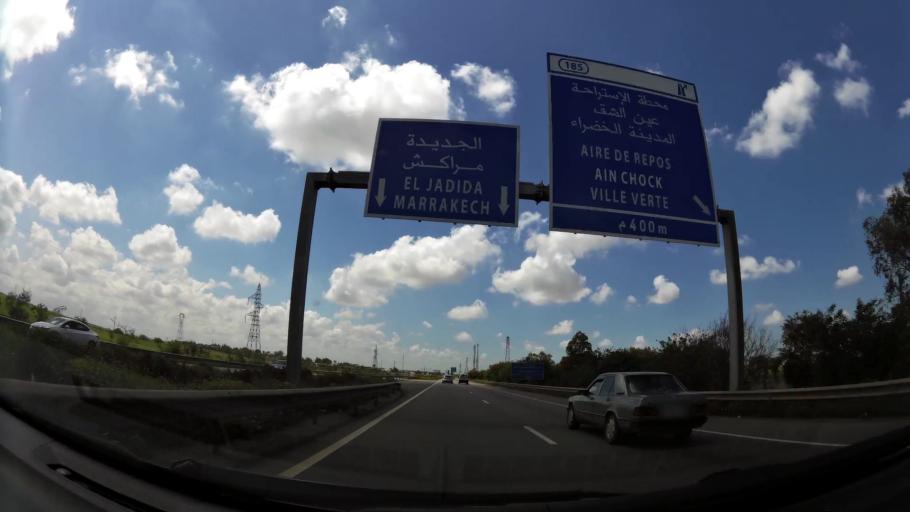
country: MA
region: Grand Casablanca
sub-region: Casablanca
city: Casablanca
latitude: 33.5130
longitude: -7.6015
